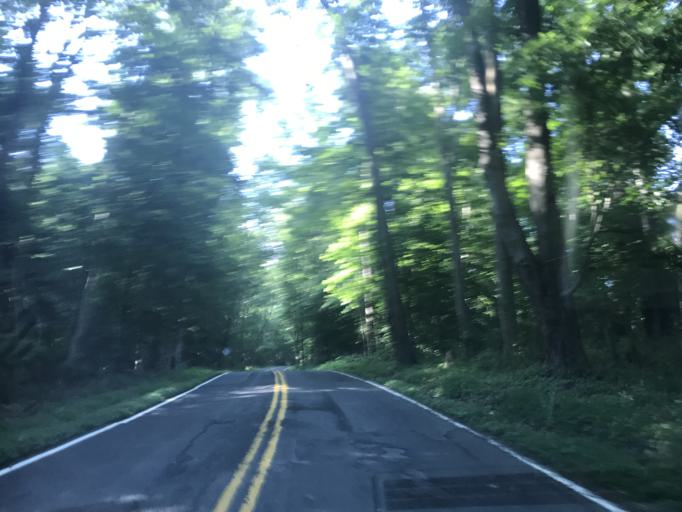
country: US
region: Maryland
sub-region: Harford County
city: Aberdeen
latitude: 39.5144
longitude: -76.1239
